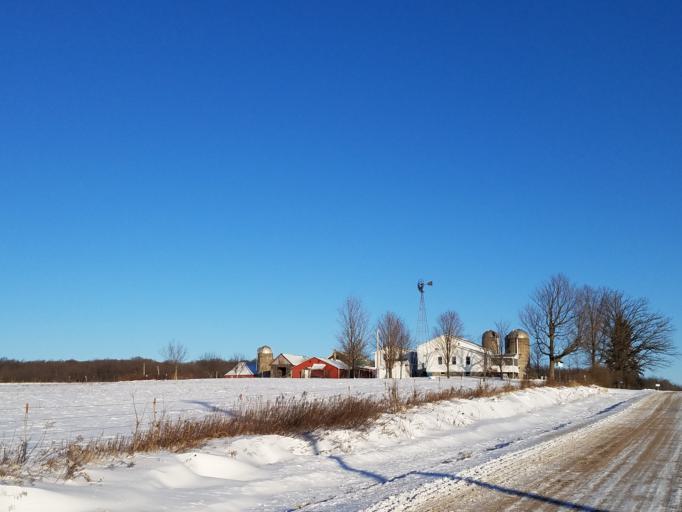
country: US
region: Wisconsin
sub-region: Clark County
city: Loyal
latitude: 44.6000
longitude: -90.4363
